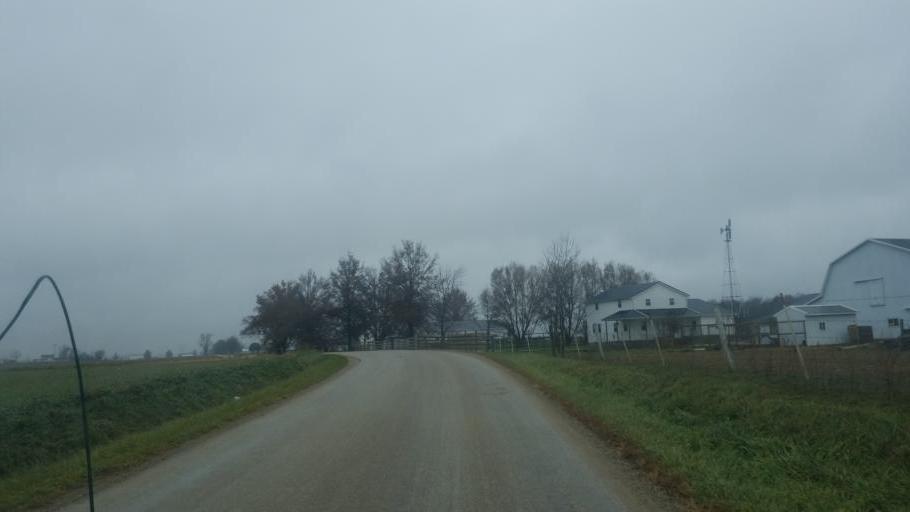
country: US
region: Indiana
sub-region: Adams County
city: Berne
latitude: 40.6593
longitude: -84.9175
